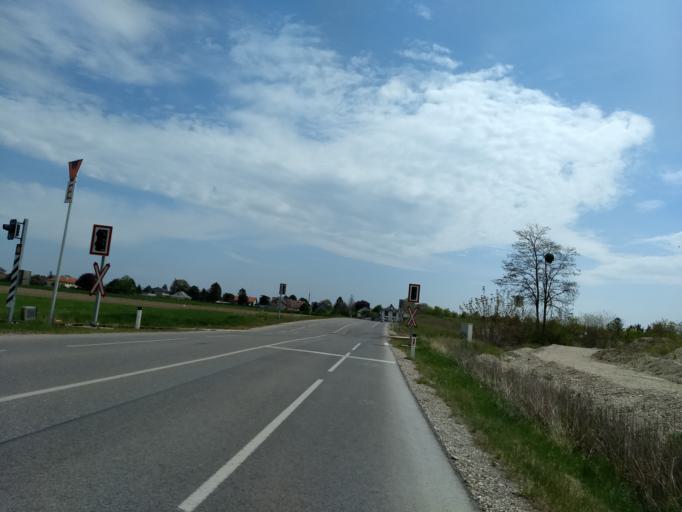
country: AT
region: Lower Austria
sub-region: Politischer Bezirk Ganserndorf
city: Gross-Enzersdorf
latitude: 48.2327
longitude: 16.5149
